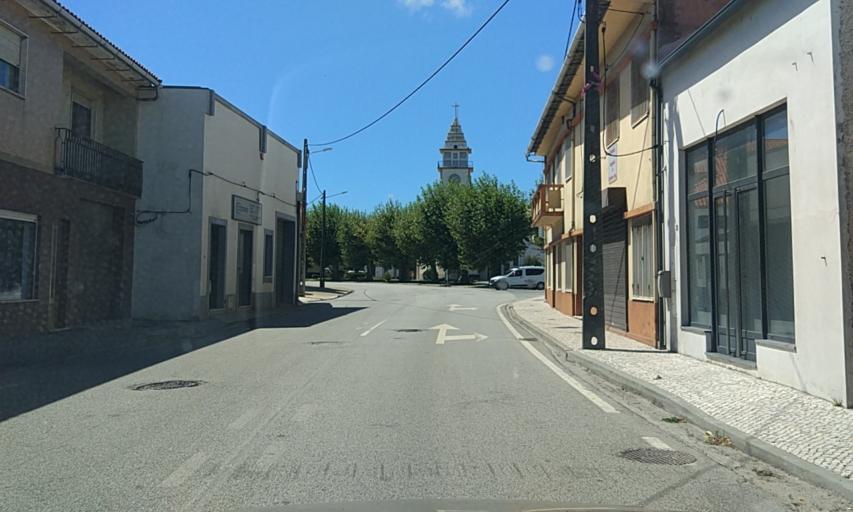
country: PT
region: Coimbra
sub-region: Mira
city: Mira
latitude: 40.4438
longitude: -8.7260
